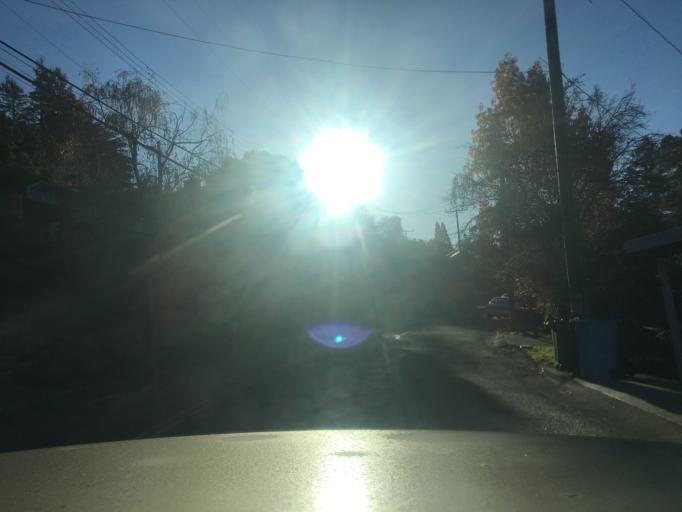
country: US
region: California
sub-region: Alameda County
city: Berkeley
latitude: 37.8857
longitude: -122.2491
